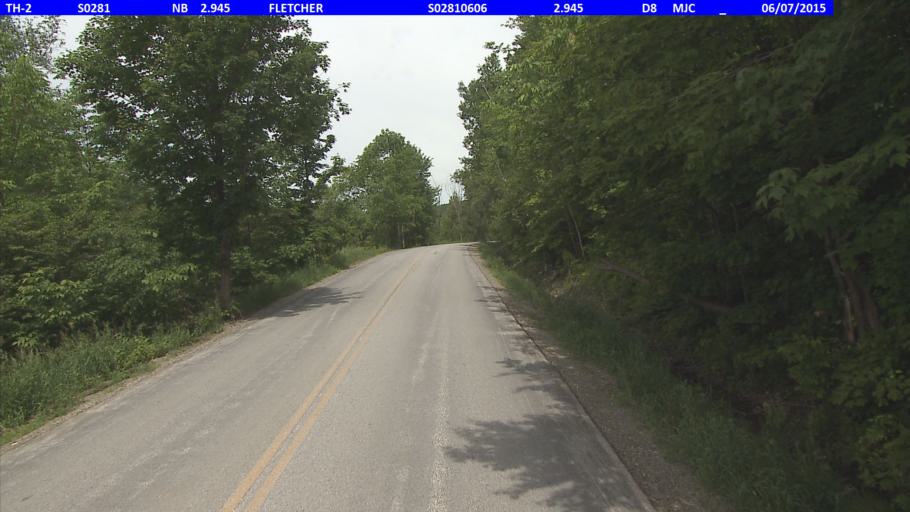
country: US
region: Vermont
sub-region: Franklin County
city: Saint Albans
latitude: 44.7102
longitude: -72.9508
